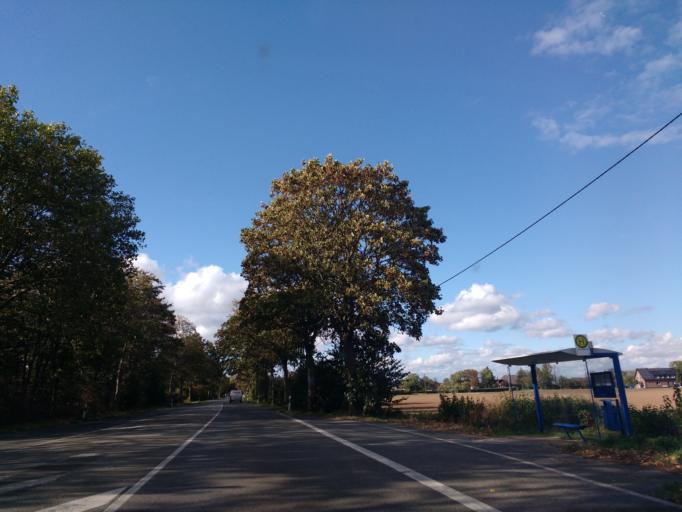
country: DE
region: North Rhine-Westphalia
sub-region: Regierungsbezirk Dusseldorf
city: Alpen
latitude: 51.5999
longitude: 6.5279
